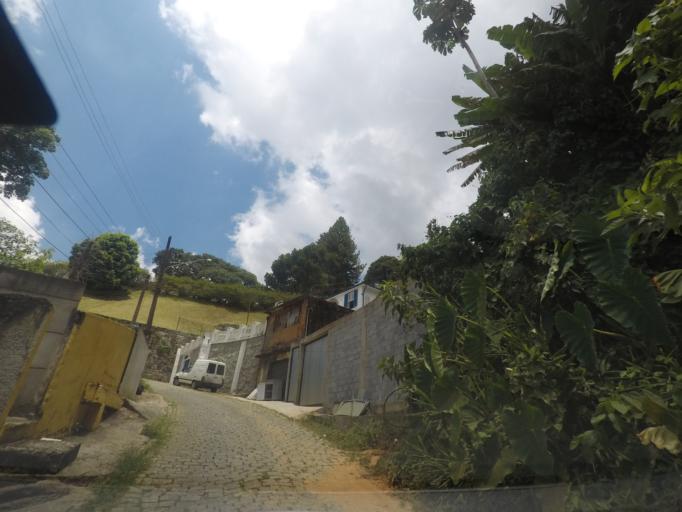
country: BR
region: Rio de Janeiro
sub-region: Petropolis
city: Petropolis
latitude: -22.4998
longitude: -43.1880
